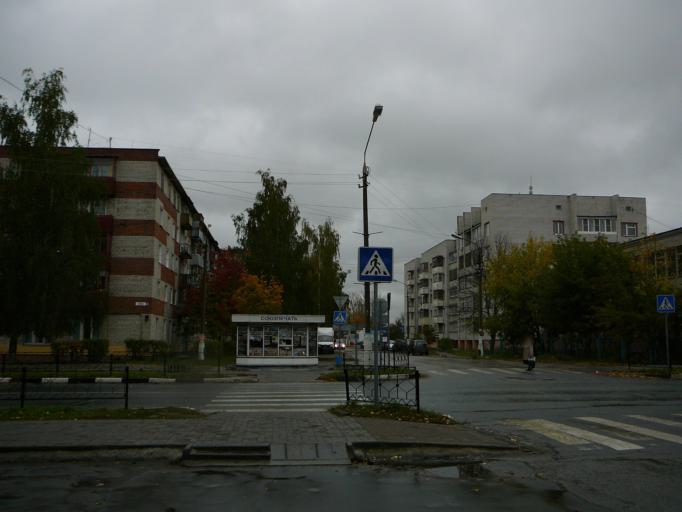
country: RU
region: Moskovskaya
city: Shatura
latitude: 55.5755
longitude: 39.5418
